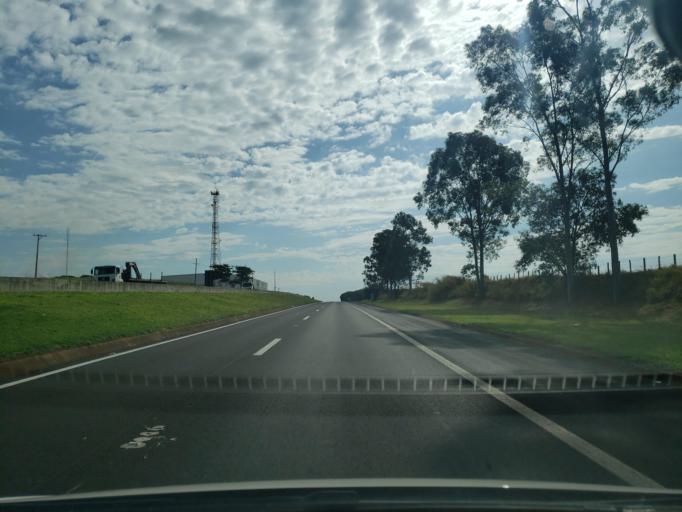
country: BR
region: Sao Paulo
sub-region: Lins
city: Lins
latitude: -21.6371
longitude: -49.8309
